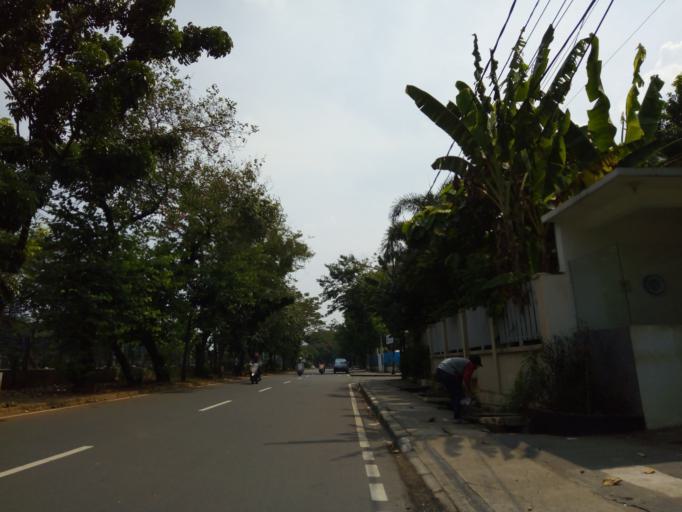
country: ID
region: Jakarta Raya
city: Jakarta
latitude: -6.2058
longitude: 106.8400
